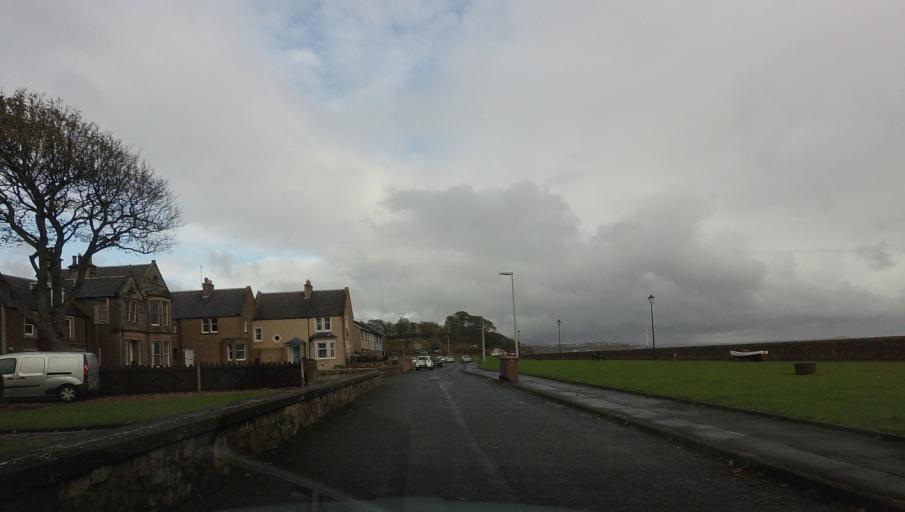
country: GB
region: Scotland
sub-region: Fife
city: East Wemyss
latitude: 56.1571
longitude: -3.0656
